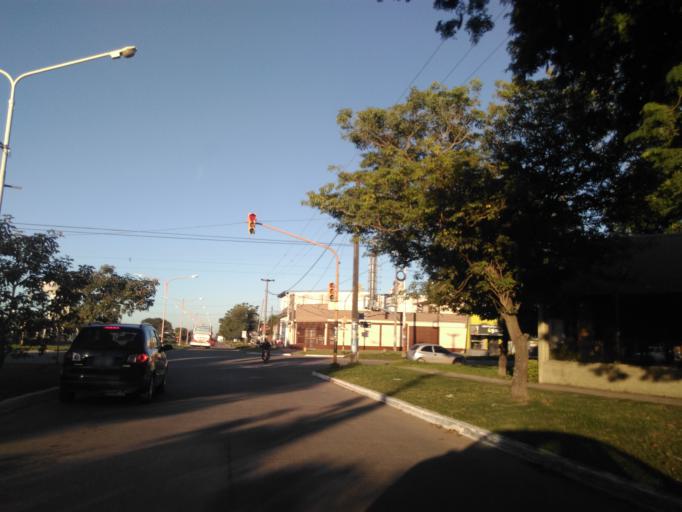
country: AR
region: Chaco
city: Resistencia
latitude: -27.4597
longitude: -59.0049
